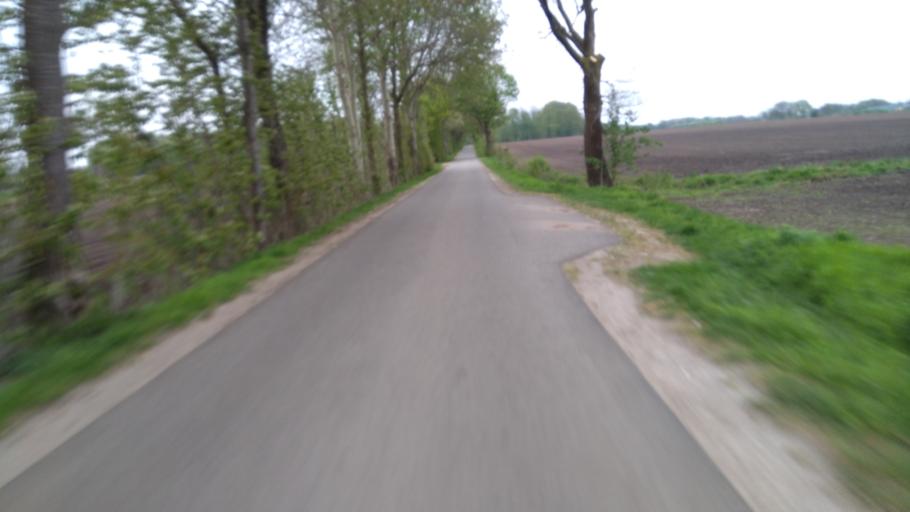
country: DE
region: Lower Saxony
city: Harsefeld
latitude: 53.4524
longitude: 9.5267
